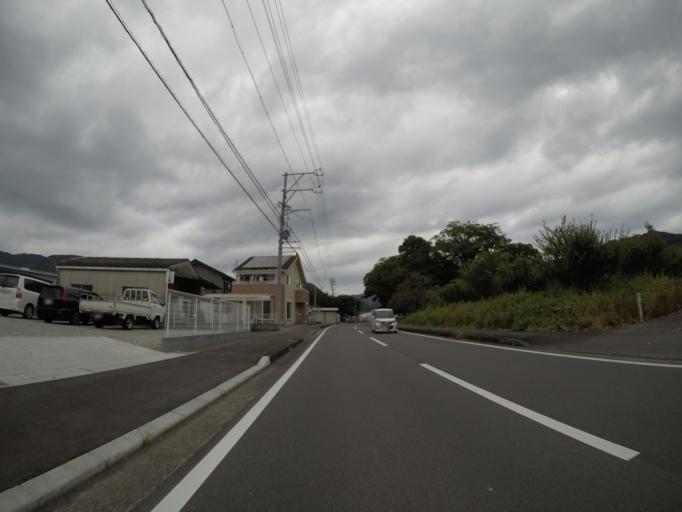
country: JP
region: Shizuoka
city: Fujieda
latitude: 34.9125
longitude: 138.2646
